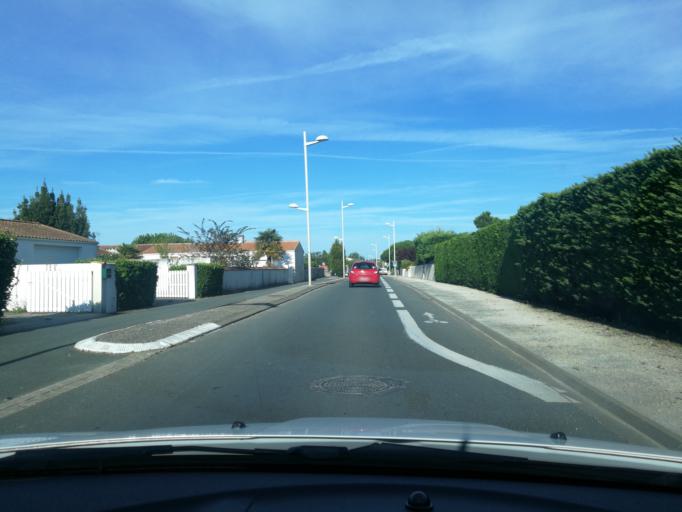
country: FR
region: Poitou-Charentes
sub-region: Departement de la Charente-Maritime
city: Dolus-d'Oleron
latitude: 45.9038
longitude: -1.2535
